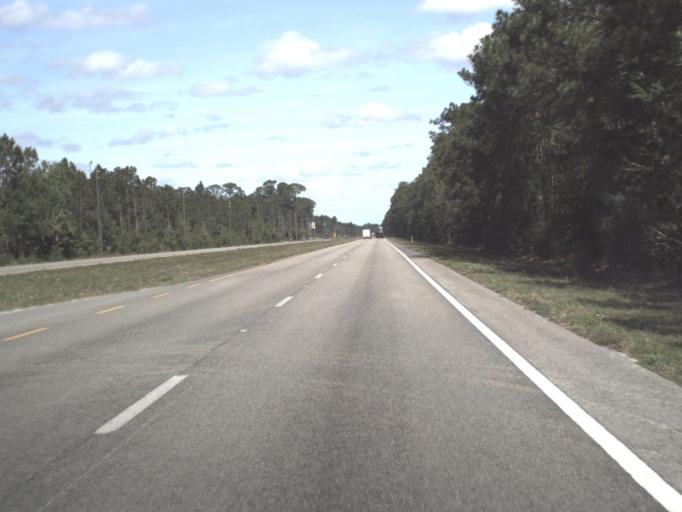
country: US
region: Florida
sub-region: Volusia County
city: Ormond-by-the-Sea
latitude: 29.3725
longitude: -81.1770
